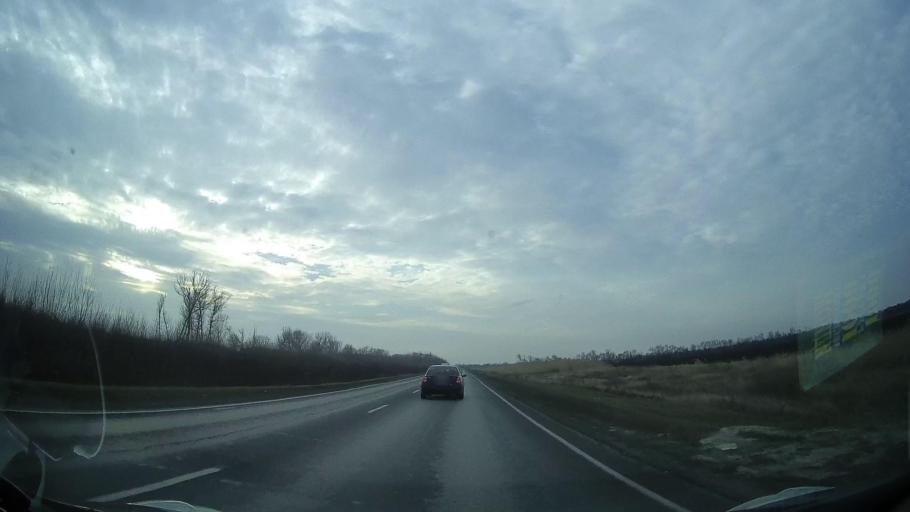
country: RU
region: Rostov
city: Starocherkasskaya
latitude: 47.1395
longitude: 40.0551
